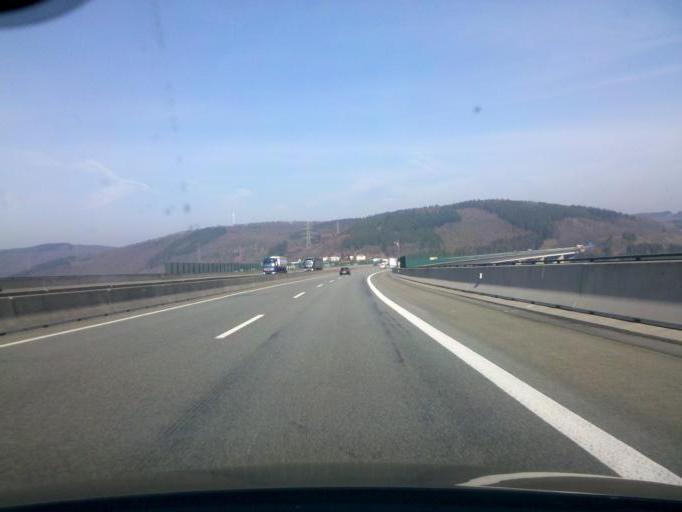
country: DE
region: North Rhine-Westphalia
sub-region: Regierungsbezirk Arnsberg
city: Siegen
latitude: 50.8445
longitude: 7.9927
